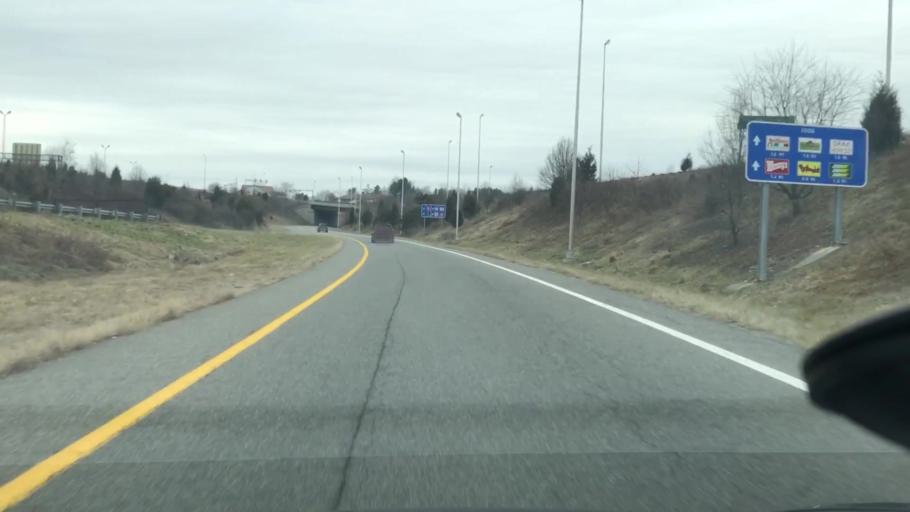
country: US
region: Virginia
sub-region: Montgomery County
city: Merrimac
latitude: 37.1916
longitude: -80.4000
